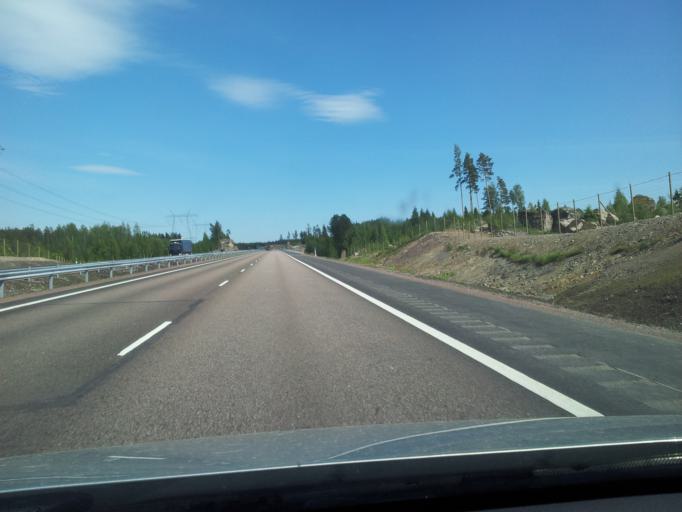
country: FI
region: Uusimaa
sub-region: Loviisa
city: Ruotsinpyhtaeae
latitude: 60.4878
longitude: 26.3661
